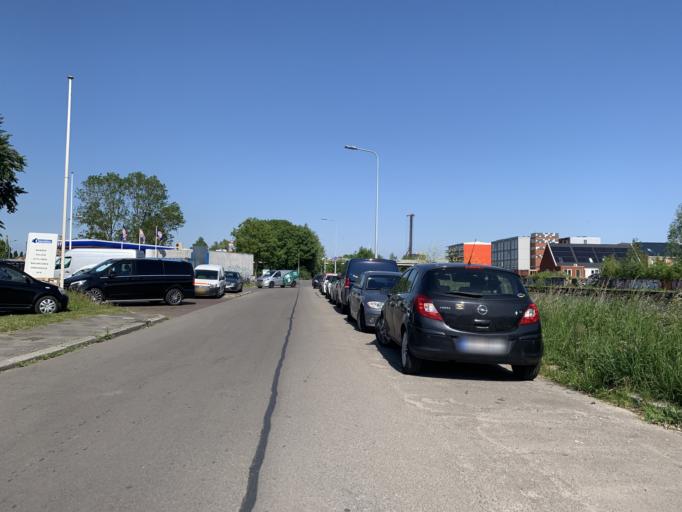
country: NL
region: Groningen
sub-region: Gemeente Groningen
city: Groningen
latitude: 53.2123
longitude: 6.5383
